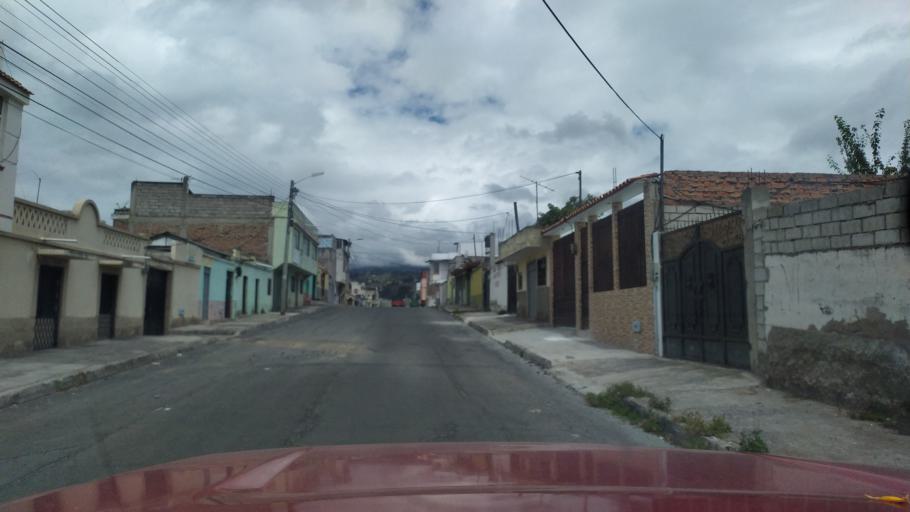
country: EC
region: Chimborazo
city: Riobamba
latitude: -1.6669
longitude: -78.6411
